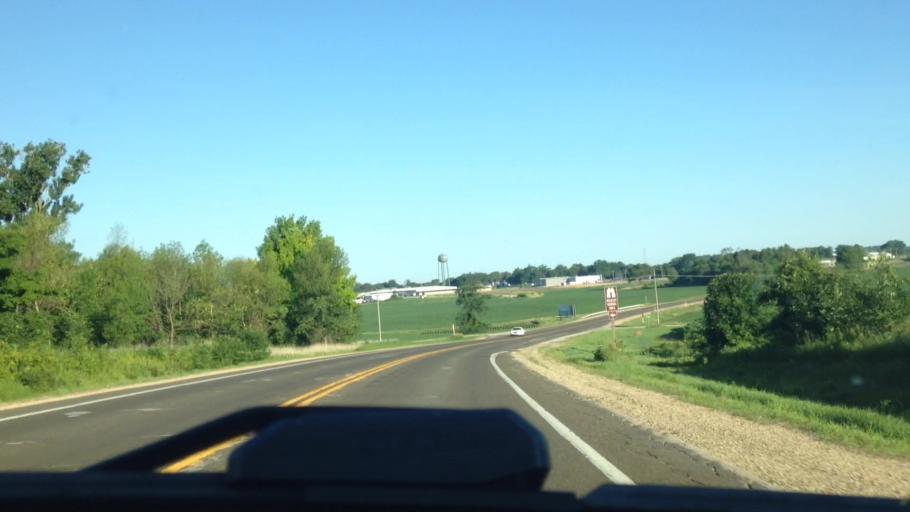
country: US
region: Wisconsin
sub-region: Columbia County
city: Poynette
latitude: 43.3326
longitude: -89.3606
